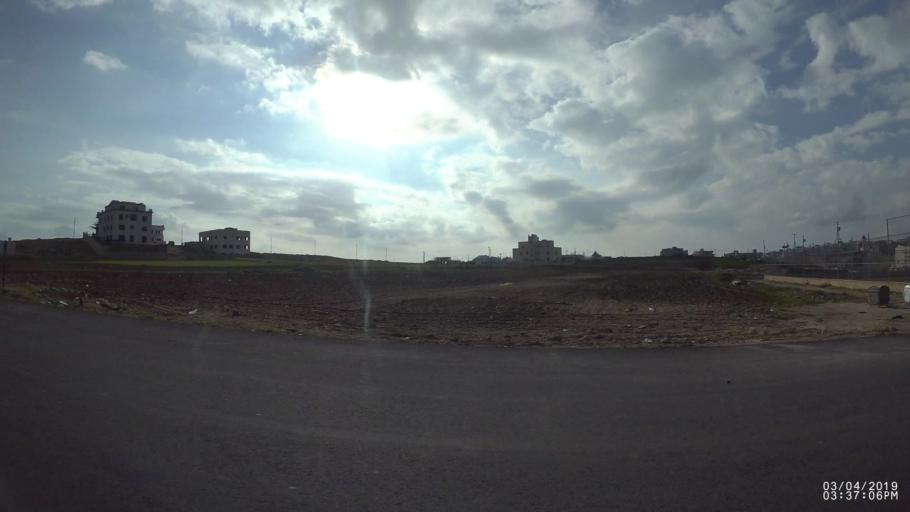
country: JO
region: Amman
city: Wadi as Sir
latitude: 31.9311
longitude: 35.8479
